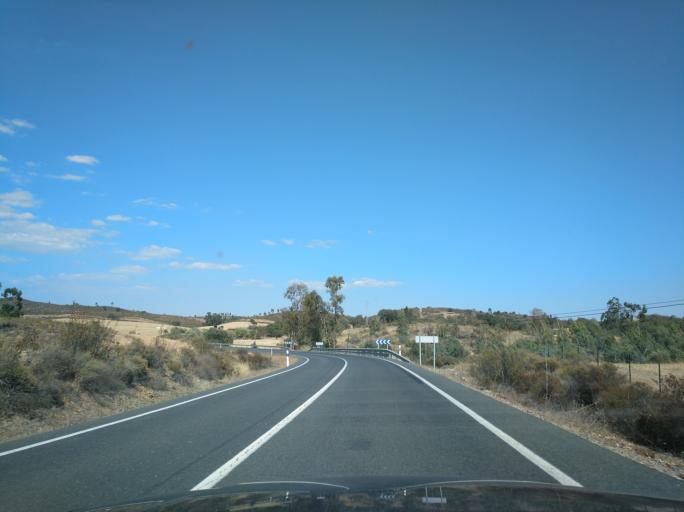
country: ES
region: Andalusia
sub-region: Provincia de Huelva
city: Alosno
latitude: 37.5683
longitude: -7.1193
